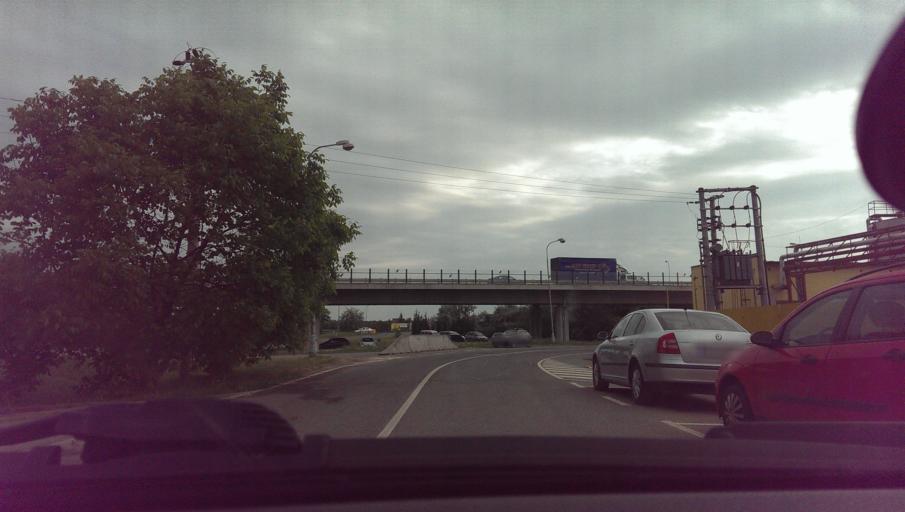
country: CZ
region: Zlin
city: Kunovice
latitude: 49.0505
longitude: 17.4691
